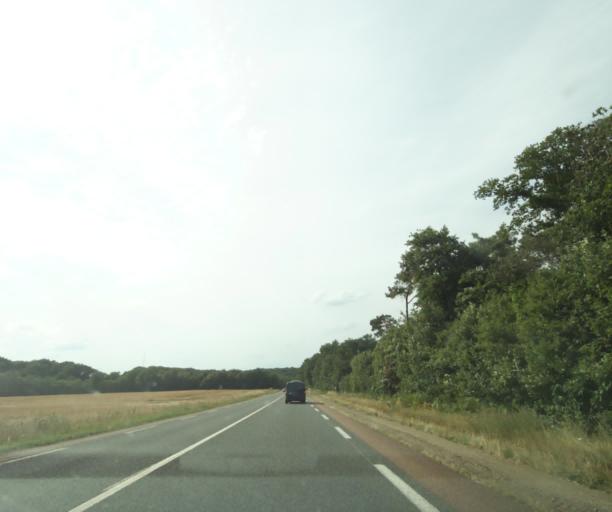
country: FR
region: Pays de la Loire
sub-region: Departement de la Sarthe
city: Luceau
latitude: 47.7533
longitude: 0.3655
